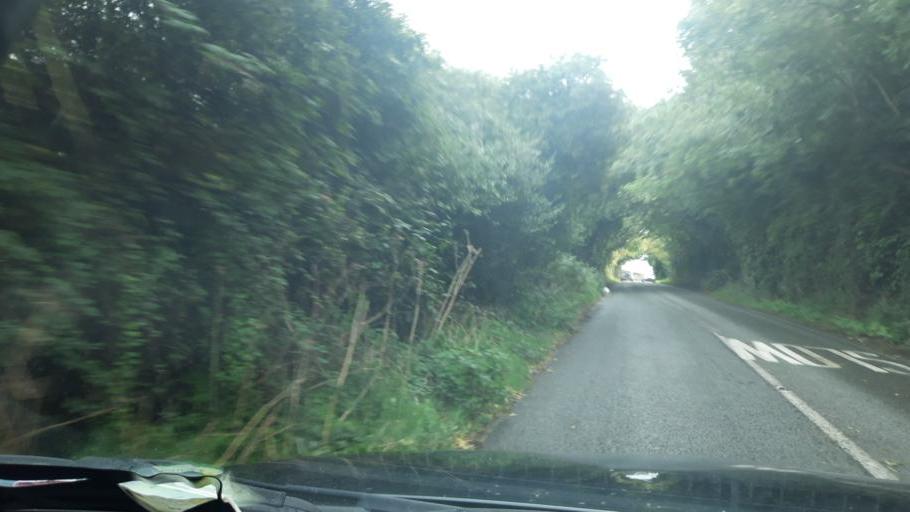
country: IE
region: Leinster
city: Ballyboden
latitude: 53.2624
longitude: -6.3221
